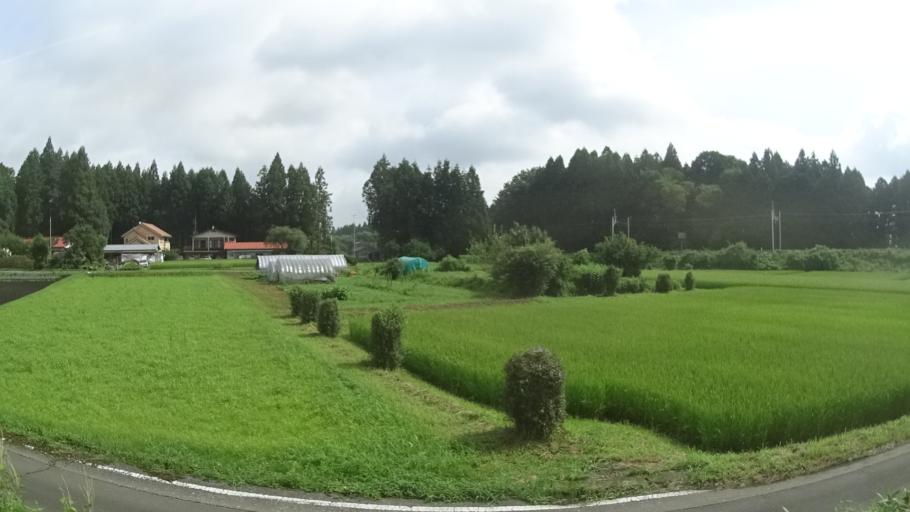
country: JP
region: Tochigi
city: Imaichi
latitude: 36.7048
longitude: 139.7077
